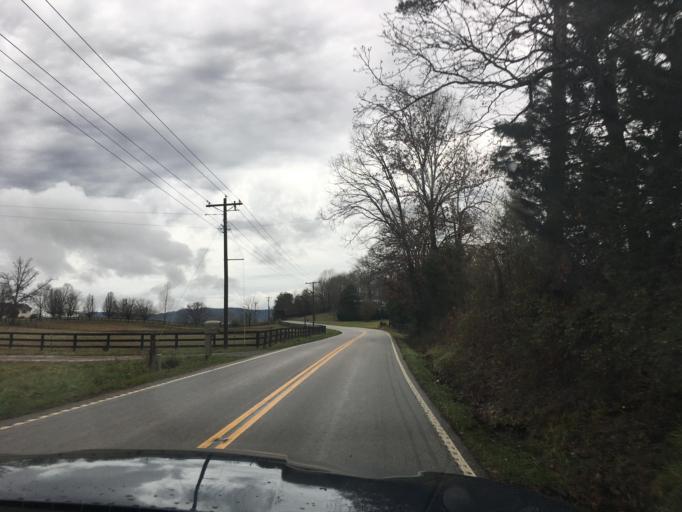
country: US
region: Tennessee
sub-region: Monroe County
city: Madisonville
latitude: 35.3591
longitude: -84.3321
